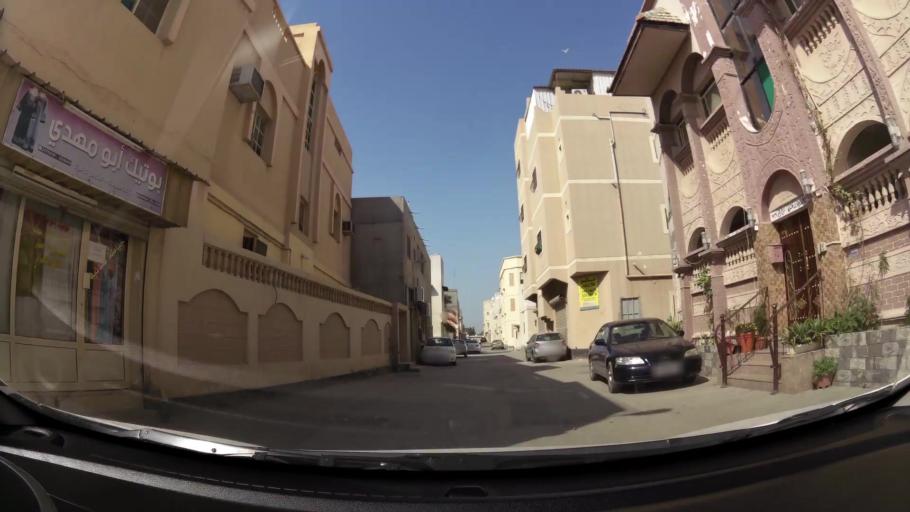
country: BH
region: Manama
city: Jidd Hafs
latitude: 26.2108
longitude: 50.4567
